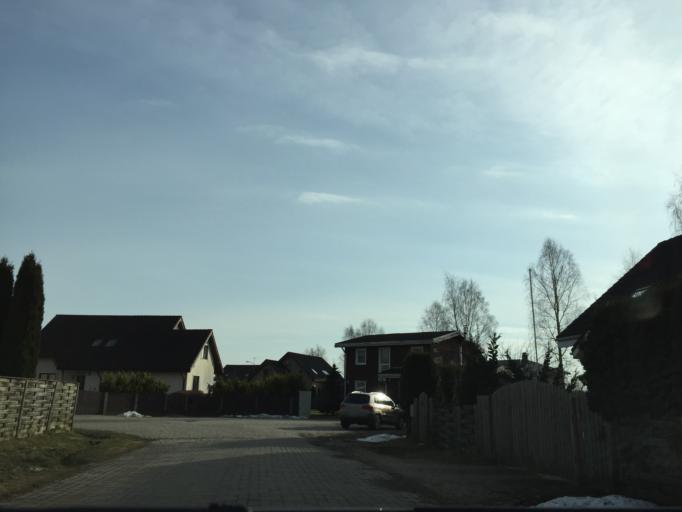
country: LV
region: Stopini
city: Ulbroka
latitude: 56.9319
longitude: 24.2583
